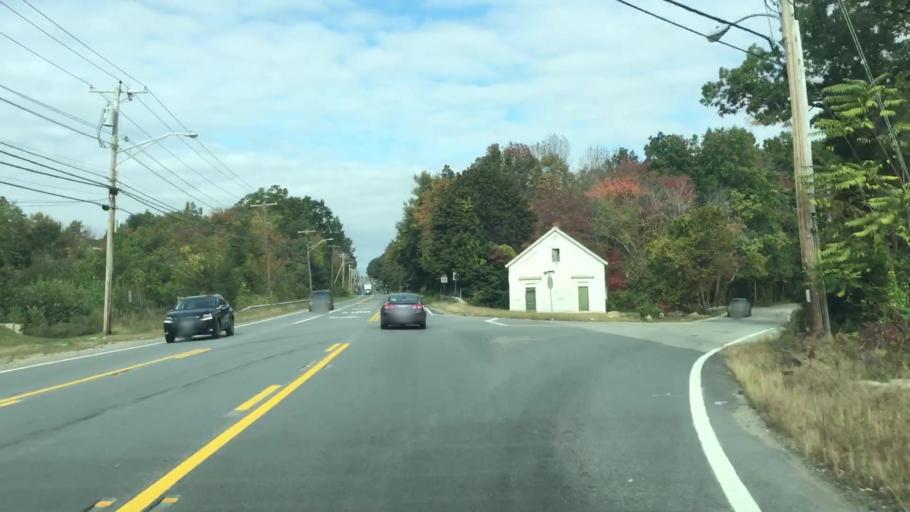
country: US
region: Massachusetts
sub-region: Essex County
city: Andover
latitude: 42.6492
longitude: -71.0927
